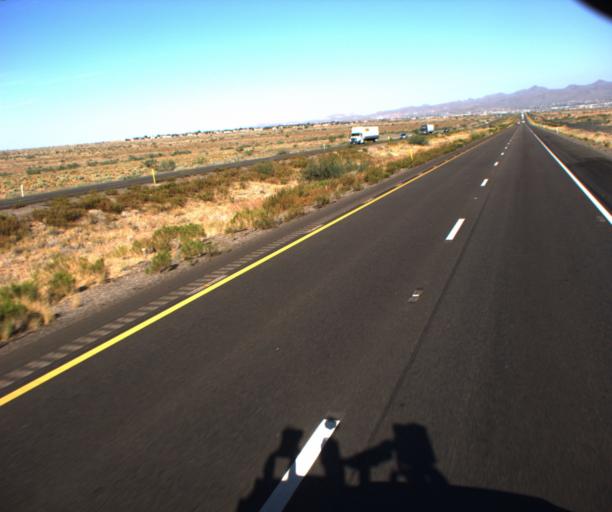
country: US
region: Arizona
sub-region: Mohave County
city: New Kingman-Butler
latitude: 35.2037
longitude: -113.9384
